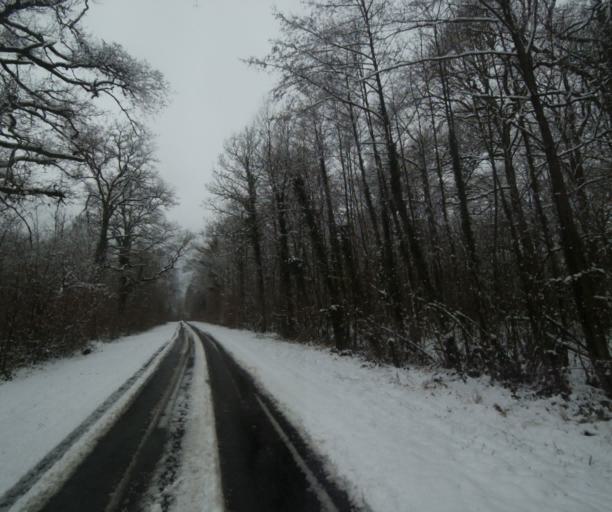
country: FR
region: Champagne-Ardenne
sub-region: Departement de la Haute-Marne
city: Wassy
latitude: 48.4640
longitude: 4.9430
